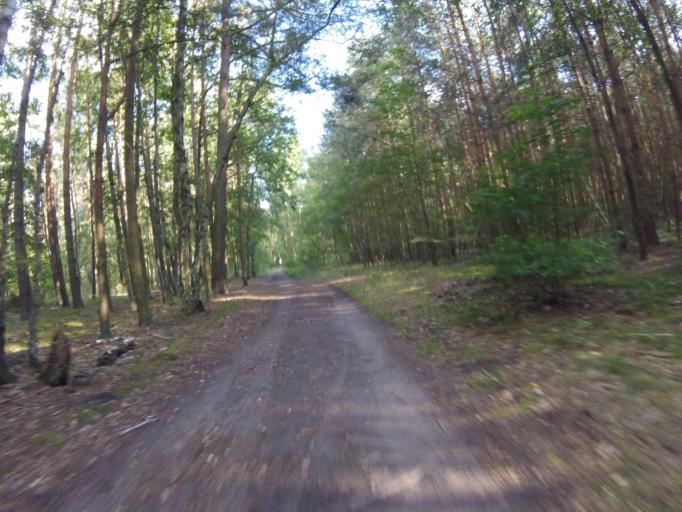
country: DE
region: Brandenburg
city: Schulzendorf
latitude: 52.3267
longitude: 13.5893
